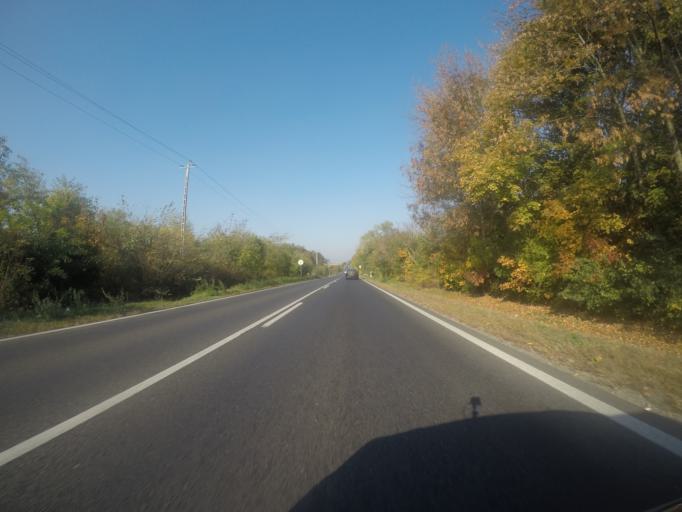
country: HU
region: Fejer
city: Baracs
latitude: 46.8512
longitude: 18.9121
